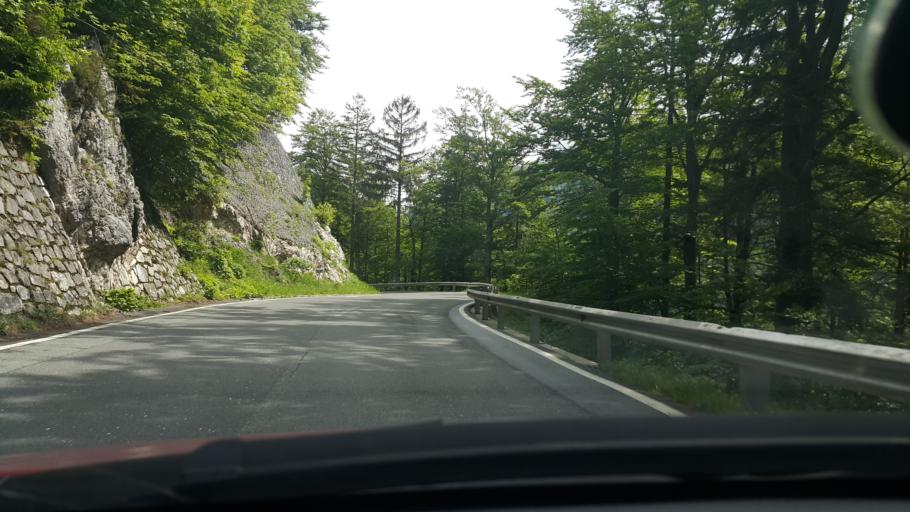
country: AT
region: Carinthia
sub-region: Politischer Bezirk Klagenfurt Land
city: Ferlach
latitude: 46.4897
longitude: 14.2754
